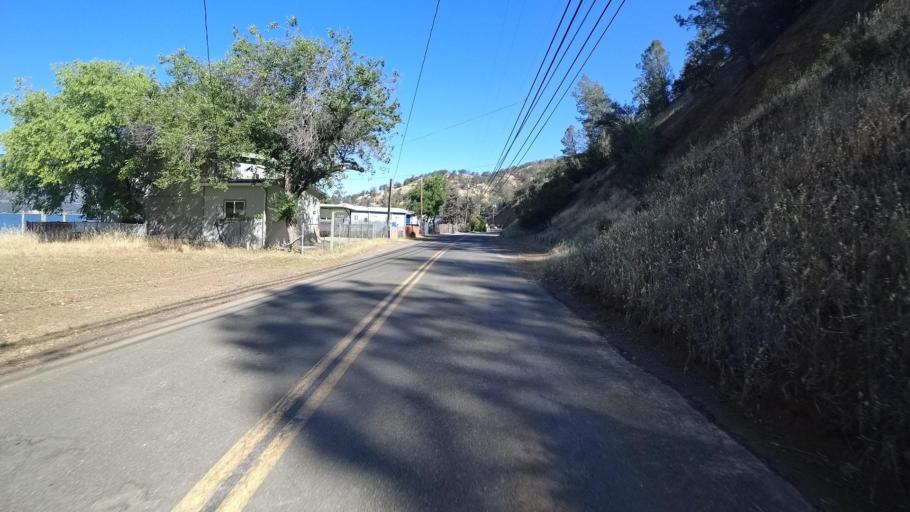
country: US
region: California
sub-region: Lake County
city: Clearlake Oaks
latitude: 38.9890
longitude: -122.6962
